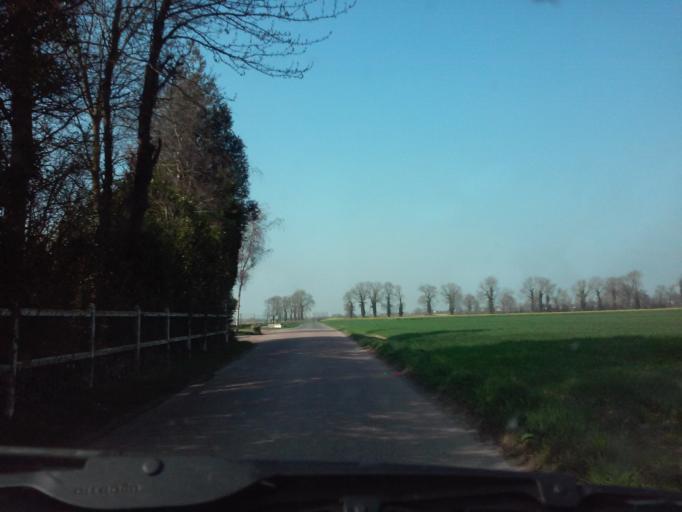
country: FR
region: Lower Normandy
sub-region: Departement du Calvados
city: Cheux
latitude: 49.1971
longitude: -0.5461
